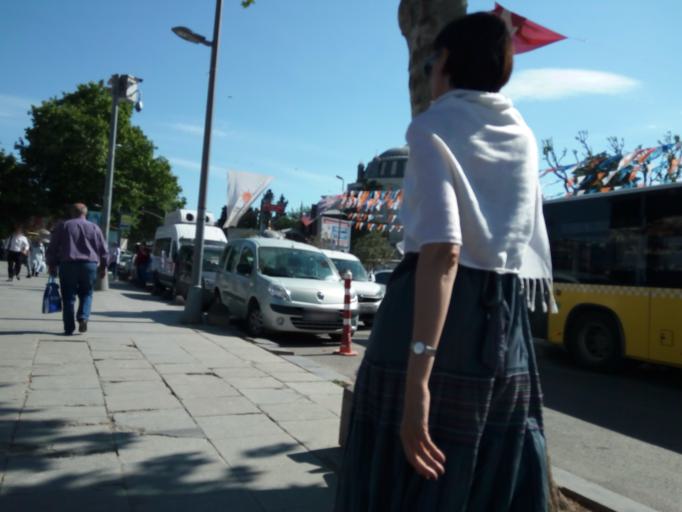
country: TR
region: Istanbul
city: UEskuedar
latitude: 41.0256
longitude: 29.0157
